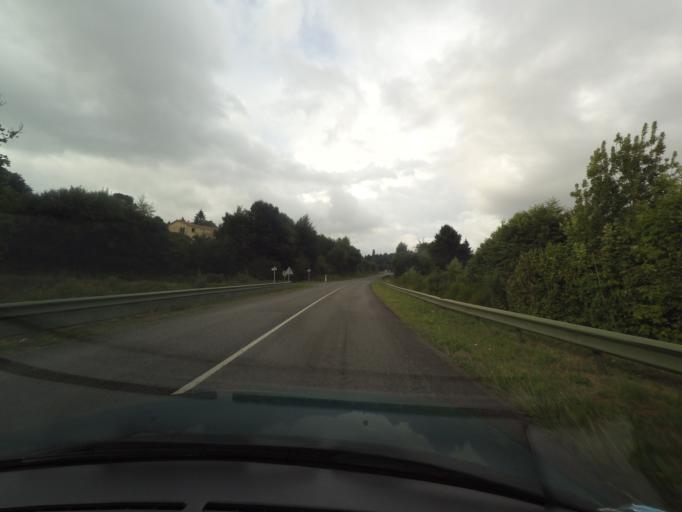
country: FR
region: Limousin
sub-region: Departement de la Haute-Vienne
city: Sereilhac
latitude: 45.7579
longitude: 1.1114
